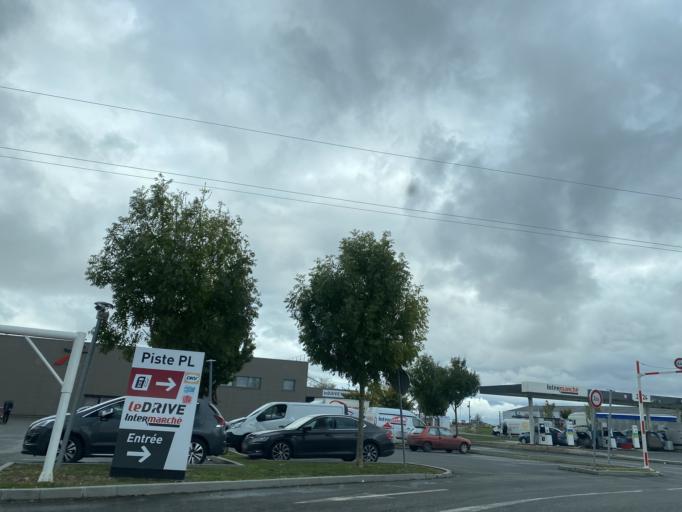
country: FR
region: Centre
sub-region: Departement du Loiret
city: Artenay
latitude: 48.0817
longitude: 1.8644
